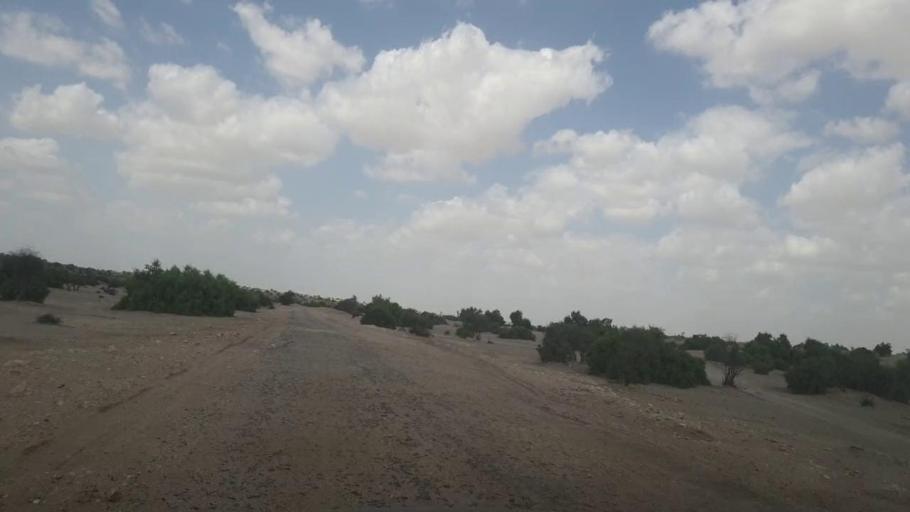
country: PK
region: Sindh
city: Kot Diji
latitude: 27.2796
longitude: 69.2243
